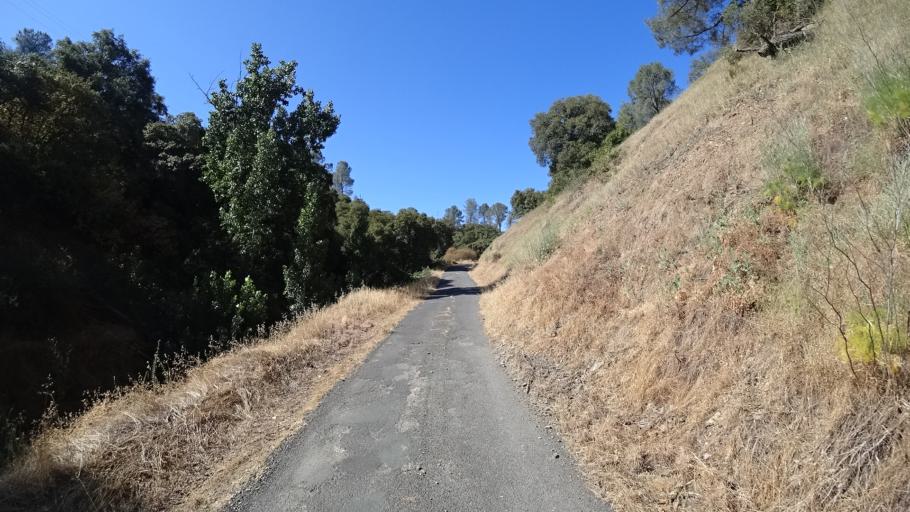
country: US
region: California
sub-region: Amador County
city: Jackson
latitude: 38.2726
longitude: -120.7593
